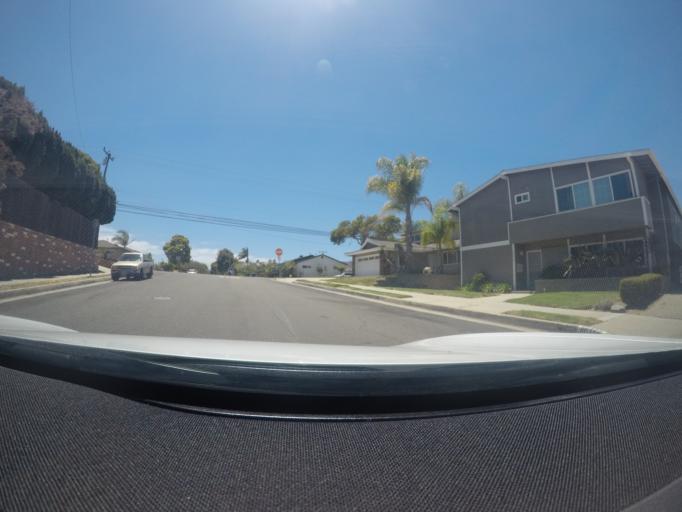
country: US
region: California
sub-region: Los Angeles County
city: Torrance
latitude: 33.8458
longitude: -118.3442
